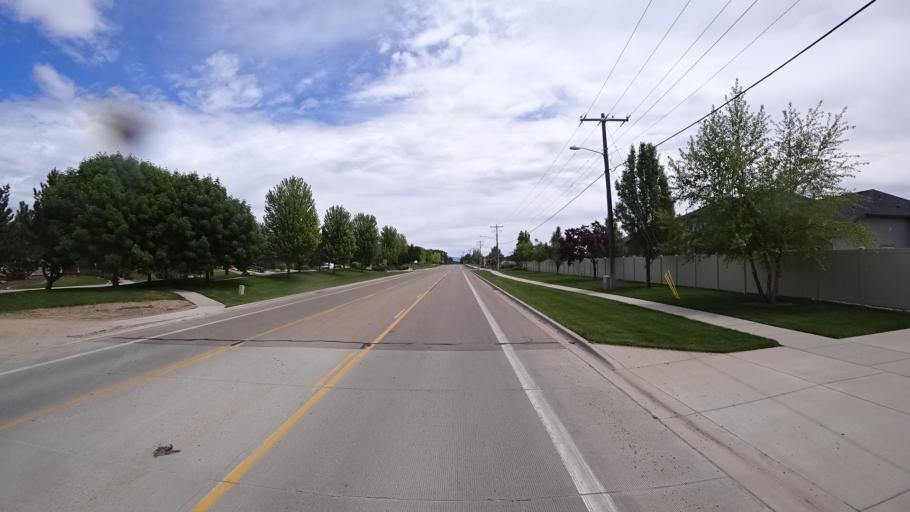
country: US
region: Idaho
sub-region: Ada County
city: Meridian
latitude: 43.5756
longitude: -116.3879
